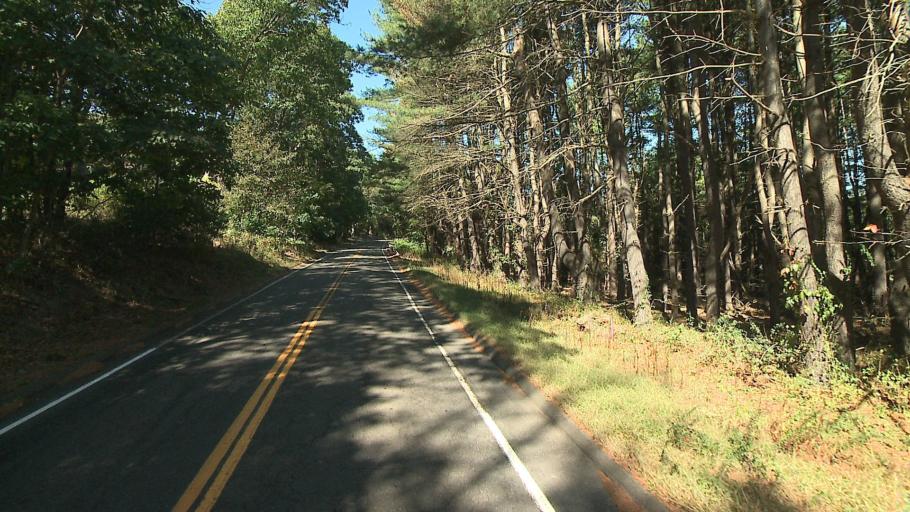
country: US
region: Connecticut
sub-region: New Haven County
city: Orange
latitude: 41.3025
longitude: -73.0185
